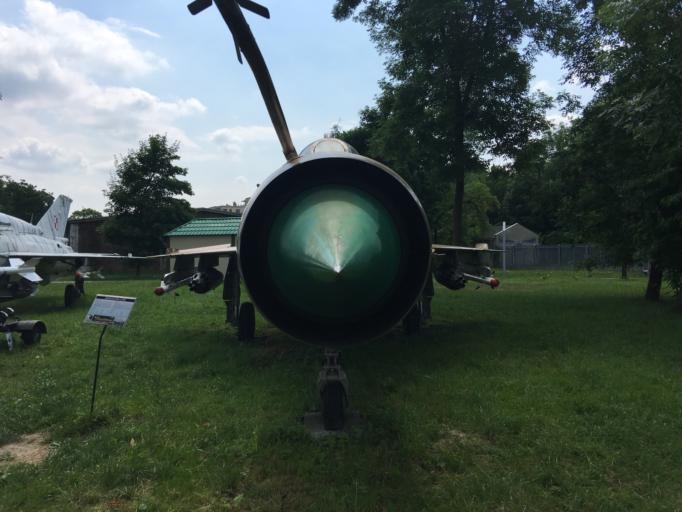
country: PL
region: Lesser Poland Voivodeship
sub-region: Krakow
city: Krakow
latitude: 50.0770
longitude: 19.9905
